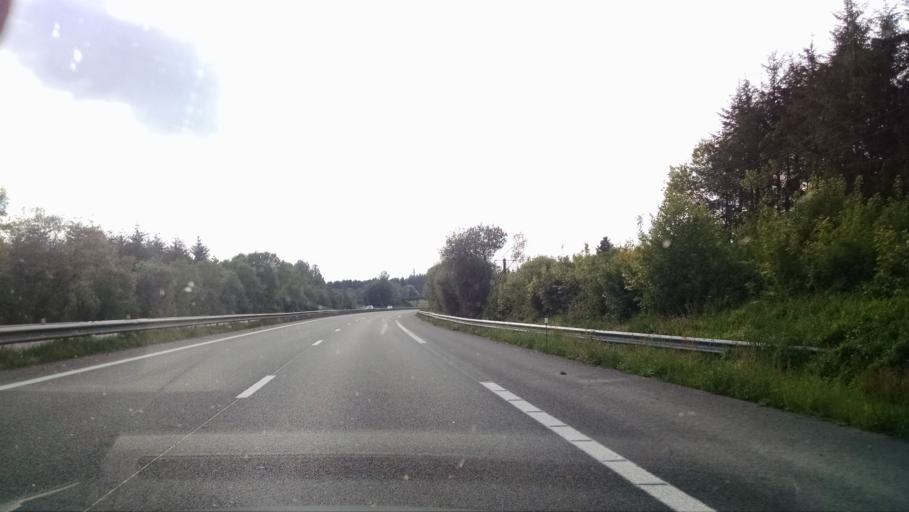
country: FR
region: Brittany
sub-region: Departement du Finistere
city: Guerlesquin
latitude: 48.5640
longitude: -3.5389
